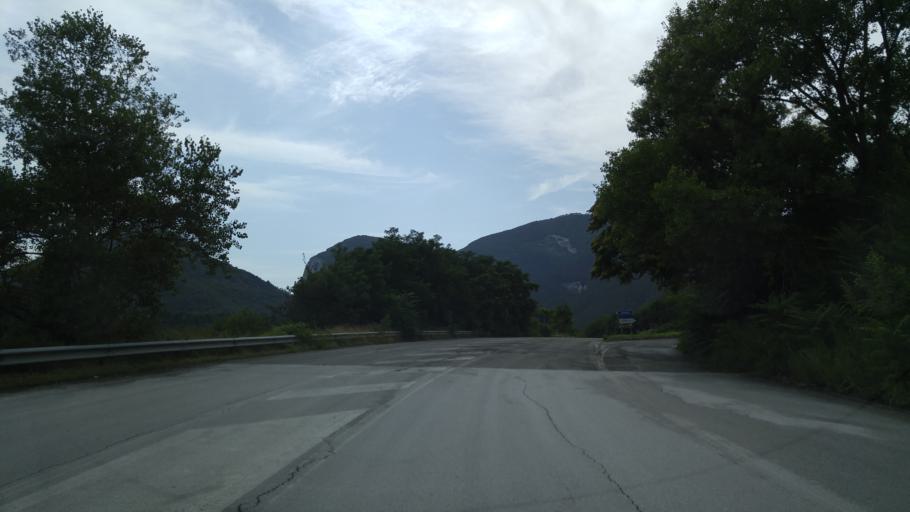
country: IT
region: The Marches
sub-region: Provincia di Pesaro e Urbino
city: Canavaccio
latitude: 43.6651
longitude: 12.7537
